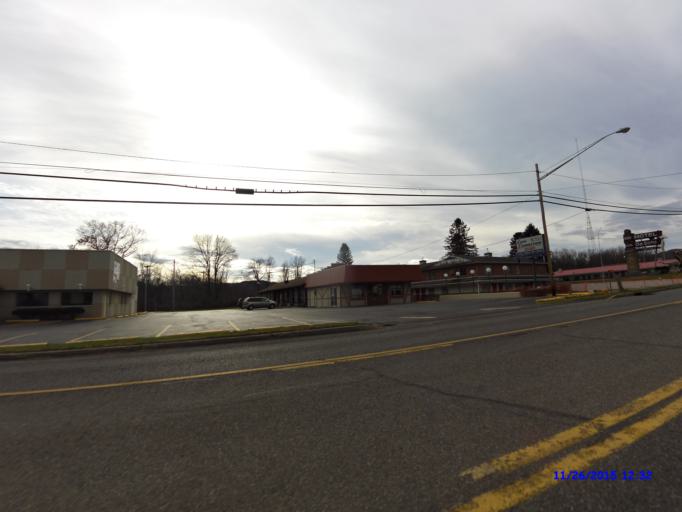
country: US
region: New York
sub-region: Cattaraugus County
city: Saint Bonaventure
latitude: 42.0770
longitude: -78.4708
